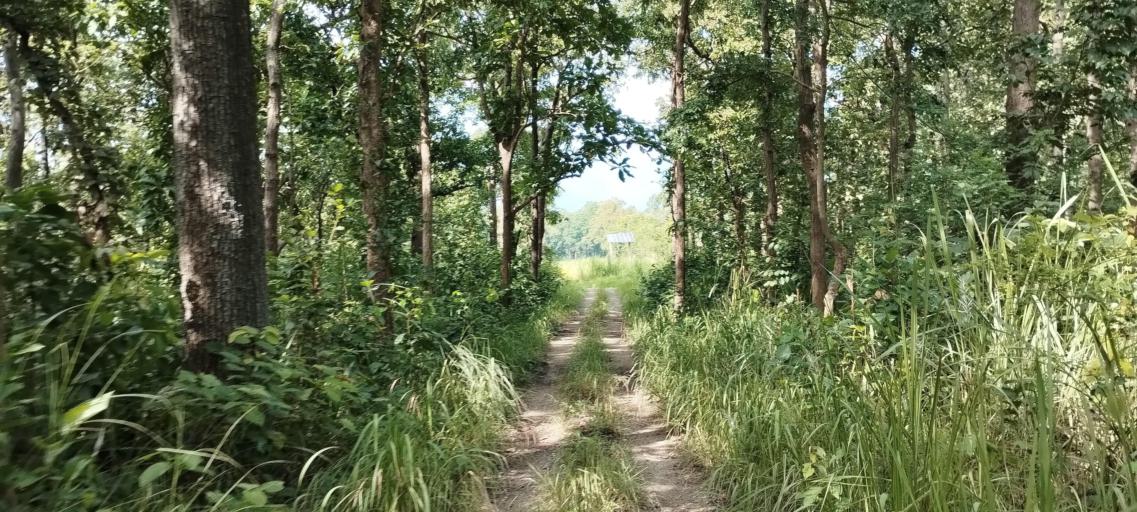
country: NP
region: Far Western
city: Tikapur
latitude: 28.5591
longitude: 81.2946
